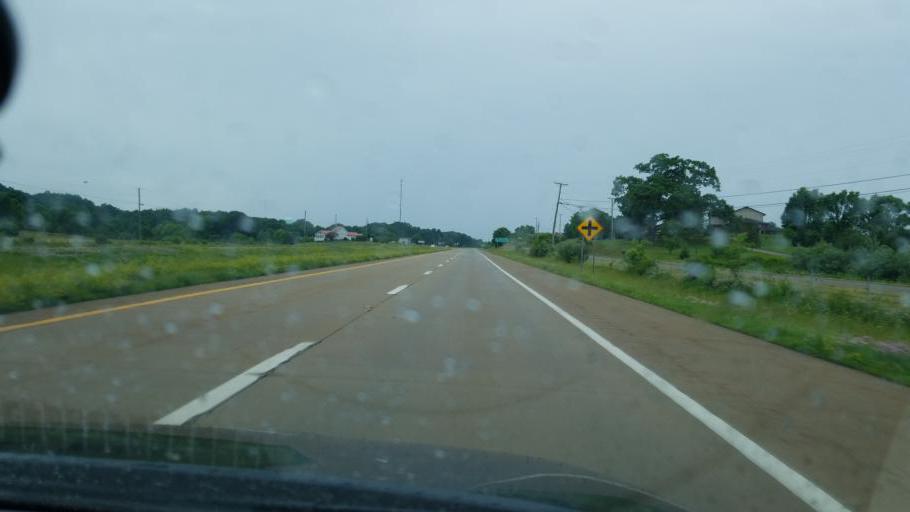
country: US
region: West Virginia
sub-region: Wood County
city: Washington
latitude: 39.2276
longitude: -81.8755
